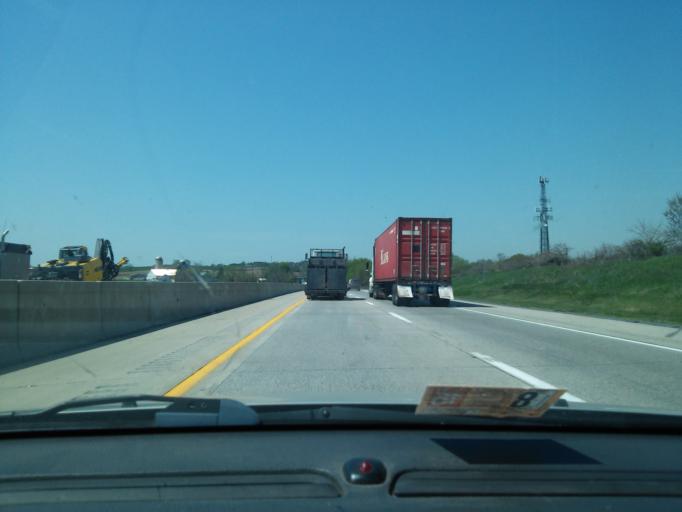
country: US
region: Pennsylvania
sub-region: Lebanon County
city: Fredericksburg
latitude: 40.4627
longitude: -76.3552
